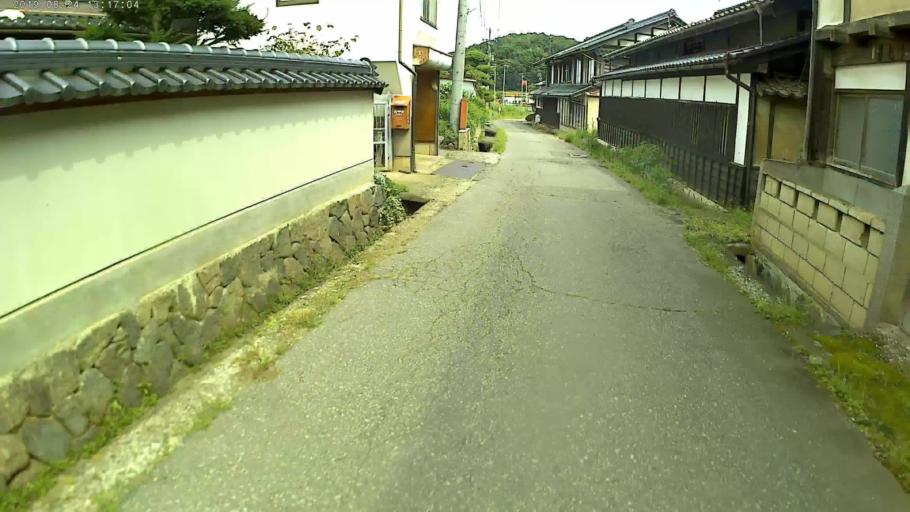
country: JP
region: Nagano
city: Komoro
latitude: 36.2692
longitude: 138.3792
